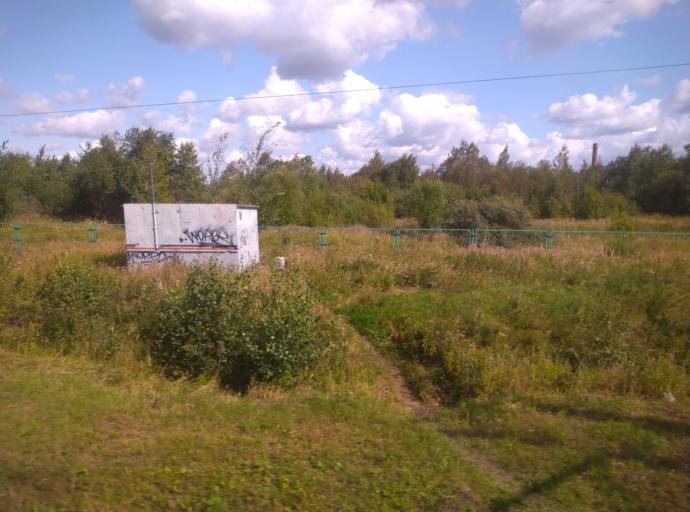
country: RU
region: St.-Petersburg
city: Kolpino
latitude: 59.7593
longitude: 30.5910
